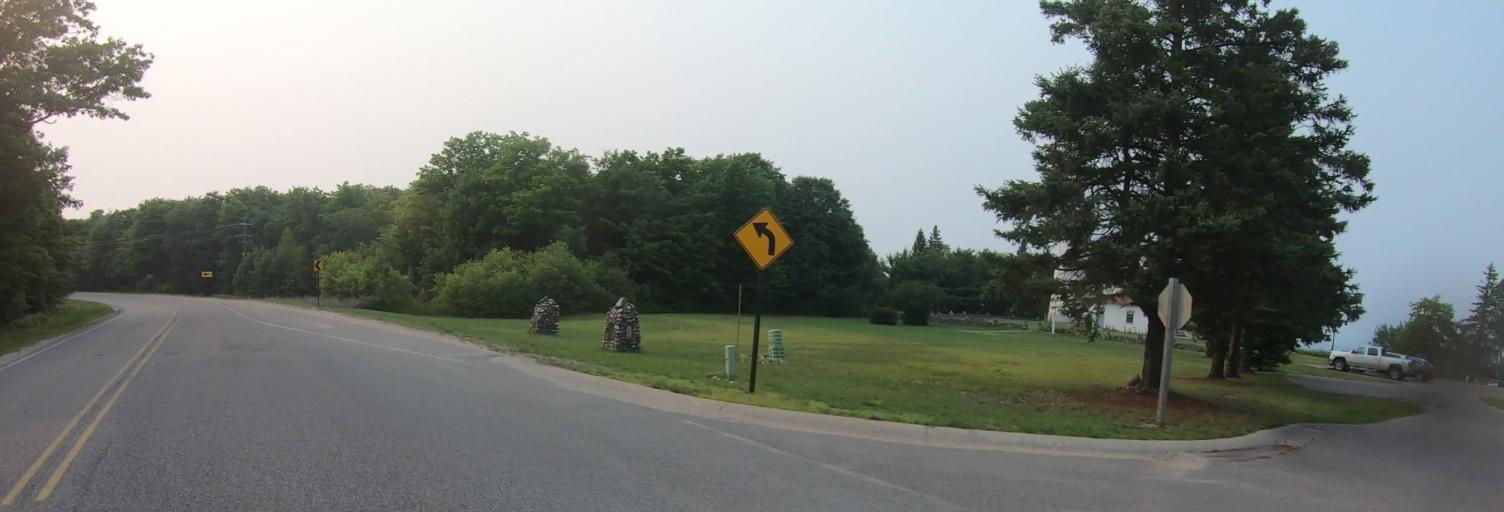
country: US
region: Michigan
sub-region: Chippewa County
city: Sault Ste. Marie
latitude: 46.4834
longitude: -84.6324
